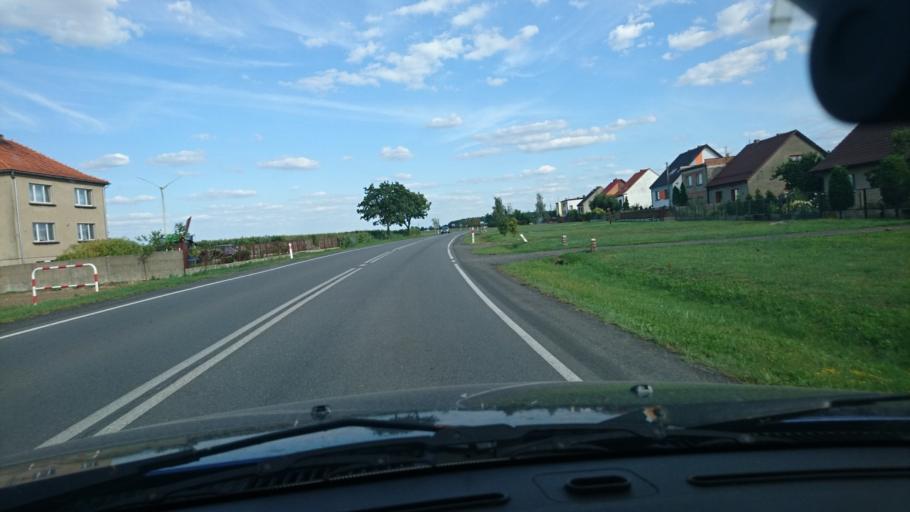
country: PL
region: Greater Poland Voivodeship
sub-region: Powiat krotoszynski
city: Kobylin
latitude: 51.7323
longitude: 17.3170
